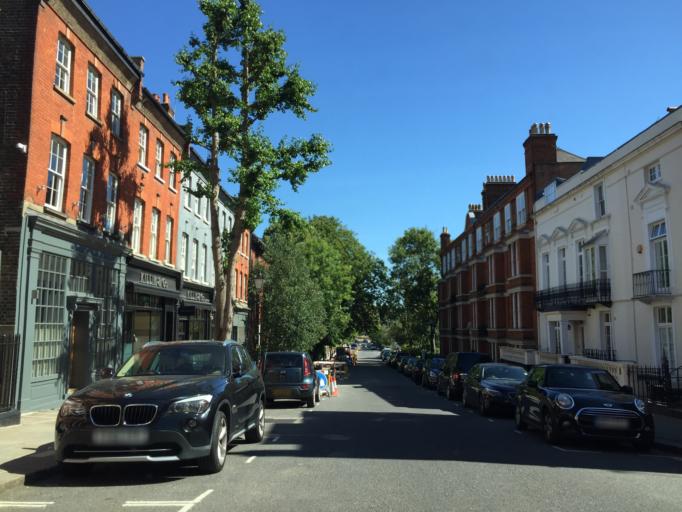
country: GB
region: England
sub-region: Greater London
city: Belsize Park
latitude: 51.5548
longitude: -0.1716
